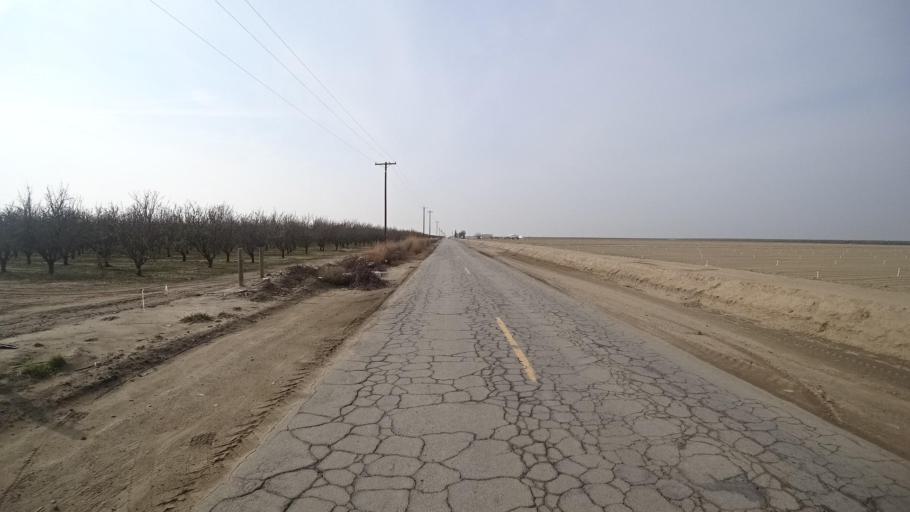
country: US
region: California
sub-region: Kern County
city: Arvin
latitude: 35.1510
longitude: -118.8377
